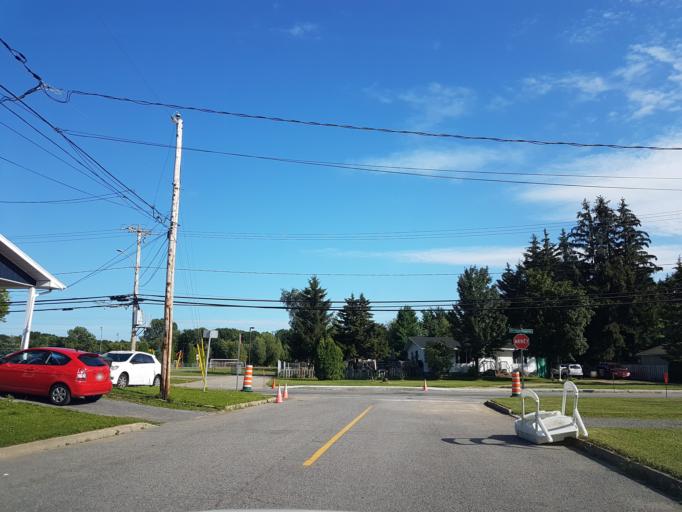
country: CA
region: Quebec
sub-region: Mauricie
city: Nicolet
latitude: 46.2886
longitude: -72.6767
